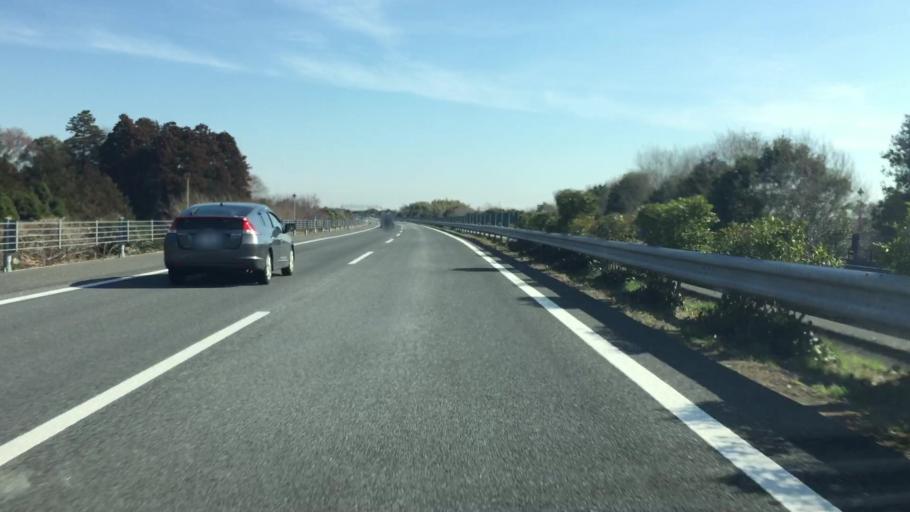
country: JP
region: Ibaraki
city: Mito-shi
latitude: 36.3193
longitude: 140.4733
